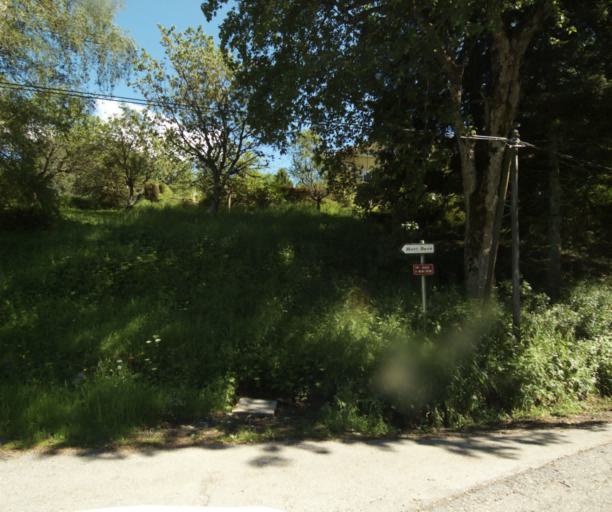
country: FR
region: Rhone-Alpes
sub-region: Departement de la Haute-Savoie
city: Bons-en-Chablais
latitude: 46.2505
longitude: 6.4004
